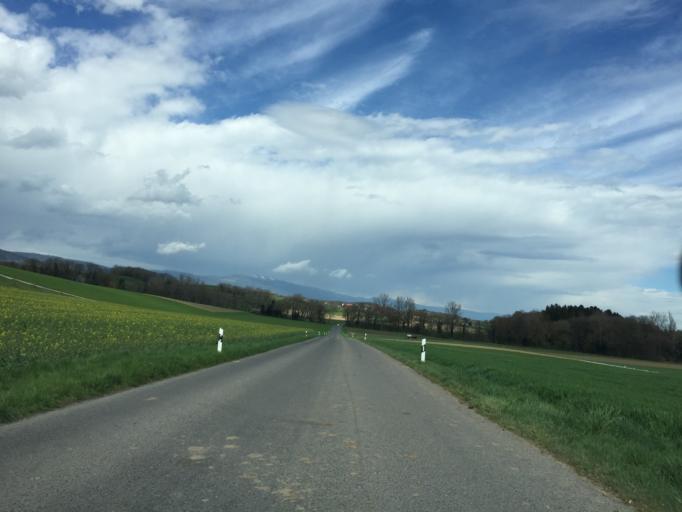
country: CH
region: Vaud
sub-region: Morges District
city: La Chaux
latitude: 46.6265
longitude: 6.4734
